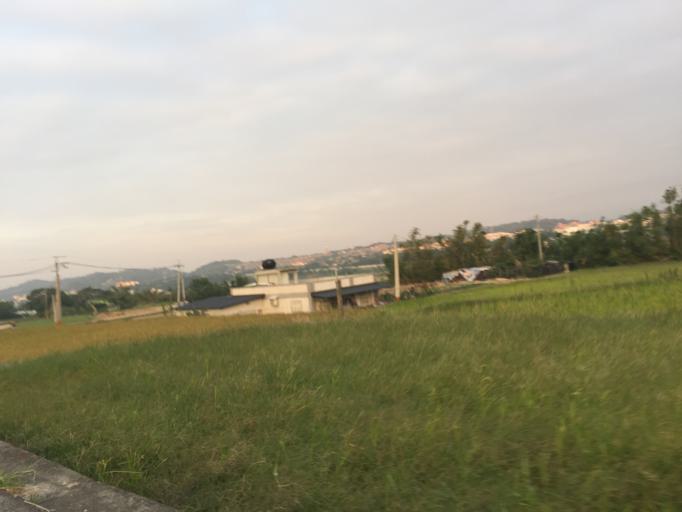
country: TW
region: Taiwan
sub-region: Miaoli
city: Miaoli
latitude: 24.4883
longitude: 120.7757
